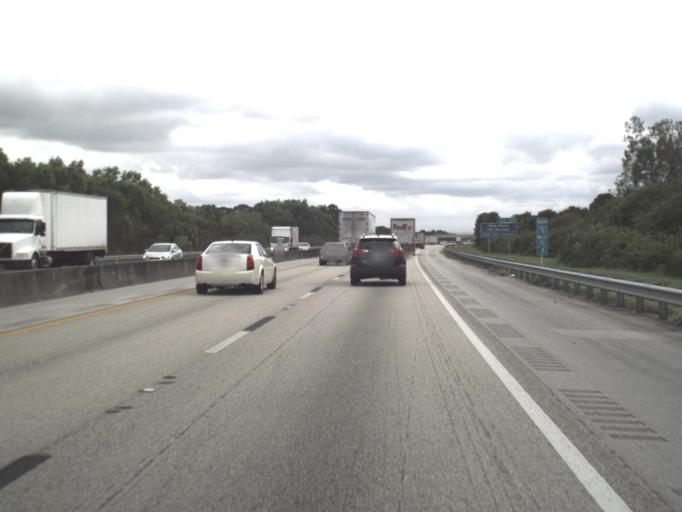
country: US
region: Florida
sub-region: Palm Beach County
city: Palm Beach Gardens
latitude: 26.8739
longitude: -80.1290
